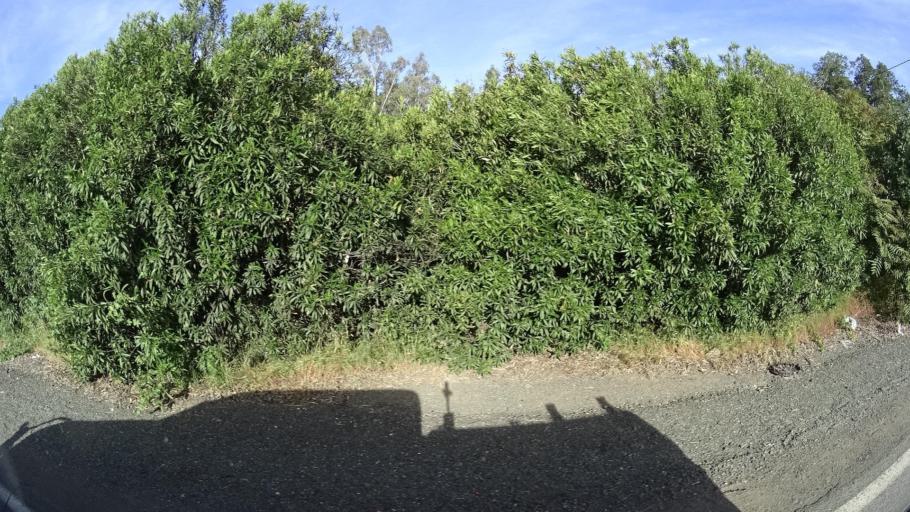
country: US
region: California
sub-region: Lake County
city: Kelseyville
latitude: 39.0035
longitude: -122.8756
